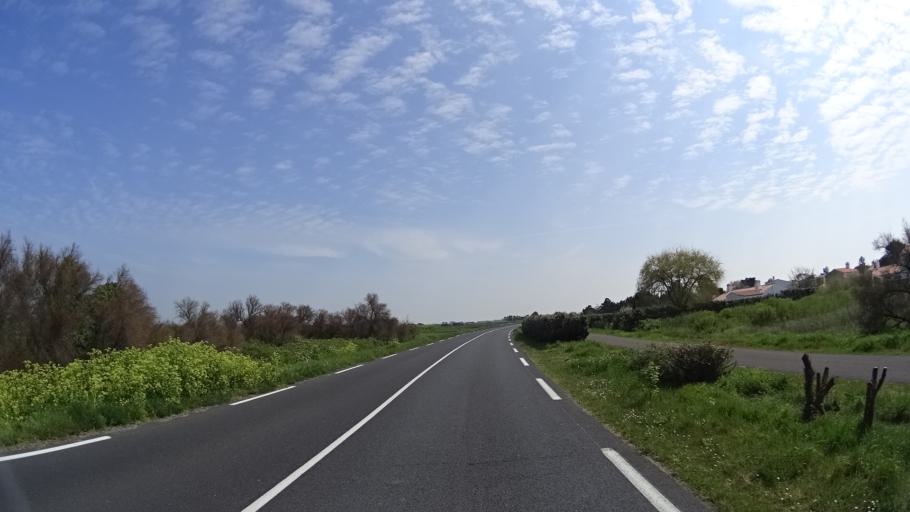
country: FR
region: Pays de la Loire
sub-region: Departement de la Vendee
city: La Gueriniere
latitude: 46.9881
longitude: -2.2841
